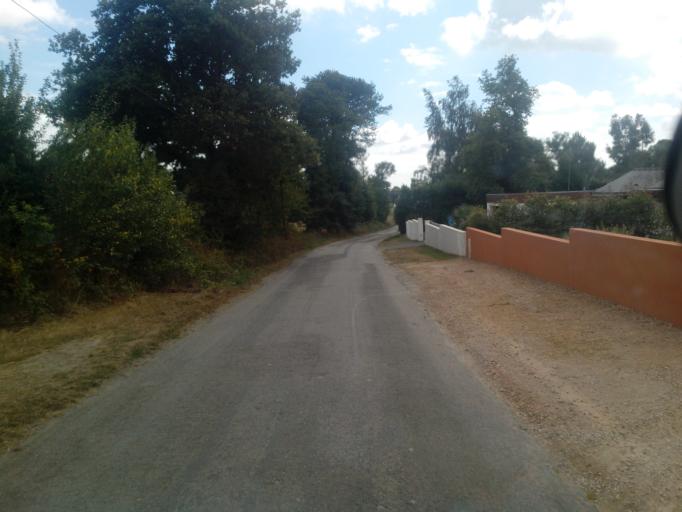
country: FR
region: Brittany
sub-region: Departement du Morbihan
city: Molac
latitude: 47.7298
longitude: -2.4247
